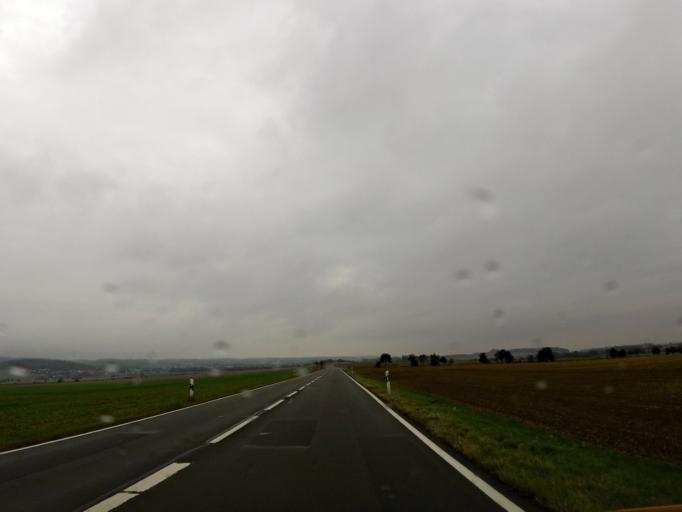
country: DE
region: Saxony-Anhalt
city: Ballenstedt
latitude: 51.7297
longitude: 11.2885
